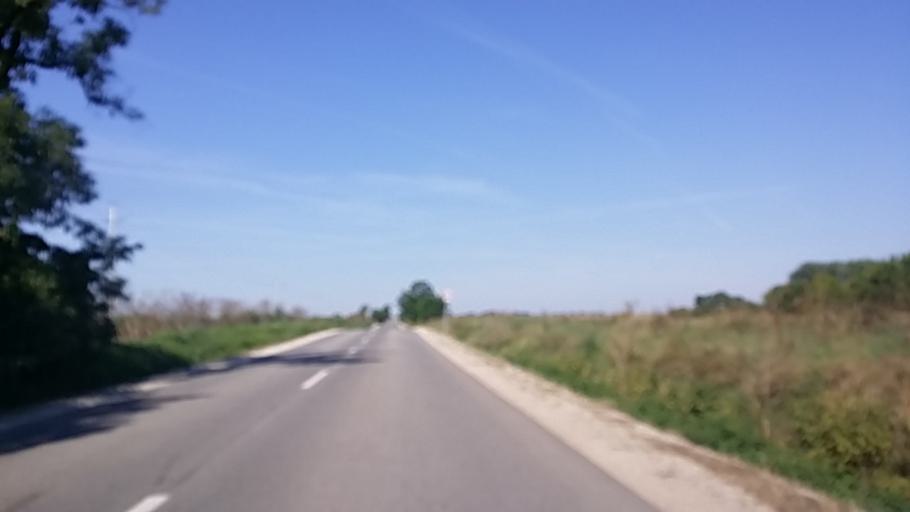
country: HU
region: Fejer
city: Pusztaszabolcs
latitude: 47.1112
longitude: 18.7638
